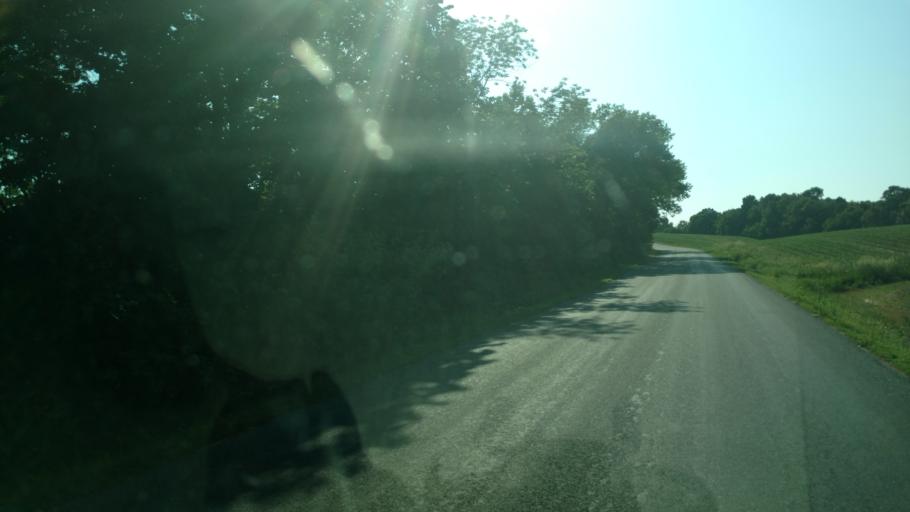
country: US
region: Wisconsin
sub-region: Vernon County
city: Hillsboro
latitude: 43.6749
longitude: -90.3607
